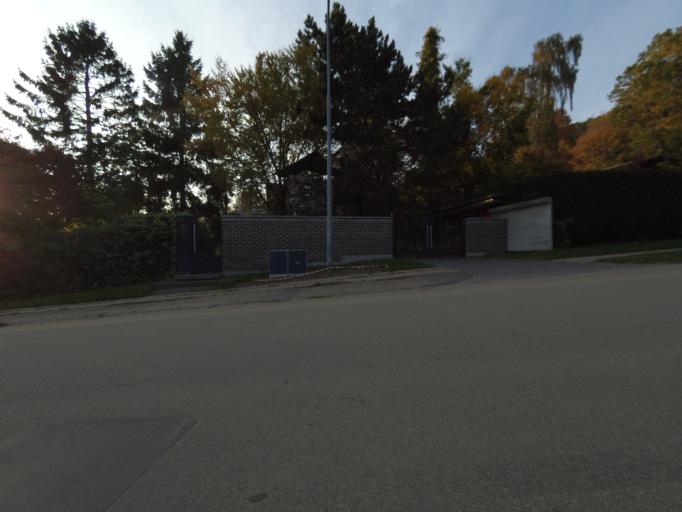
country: DK
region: Central Jutland
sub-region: Arhus Kommune
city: Stavtrup
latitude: 56.1555
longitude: 10.1181
